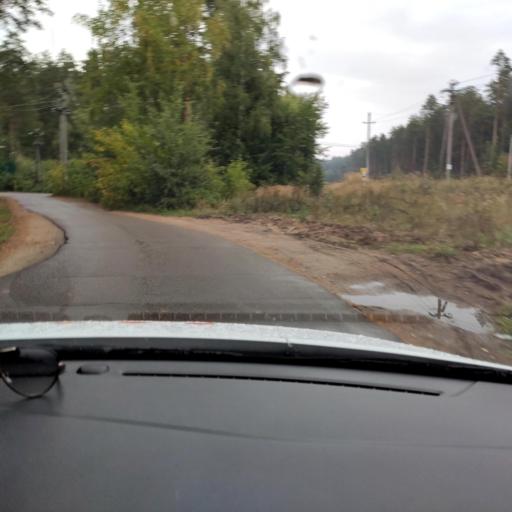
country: RU
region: Tatarstan
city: Verkhniy Uslon
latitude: 55.6421
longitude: 49.0186
